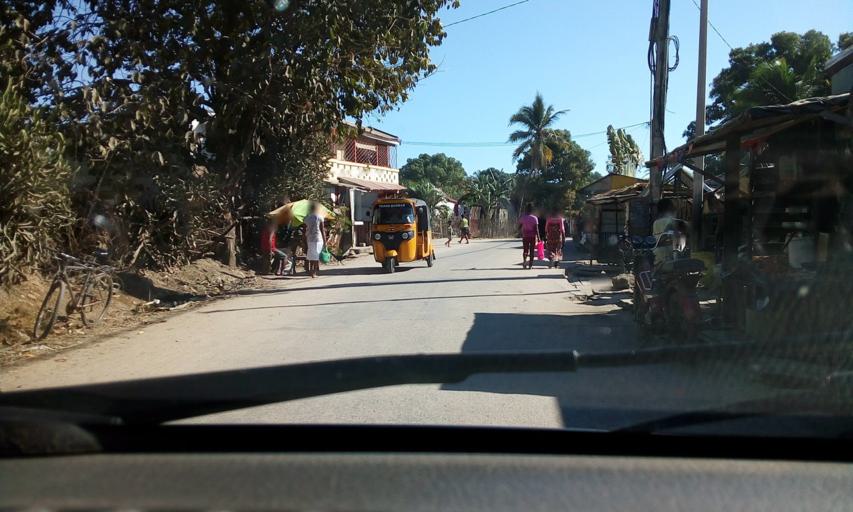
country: MG
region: Boeny
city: Mahajanga
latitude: -15.7134
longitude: 46.3386
